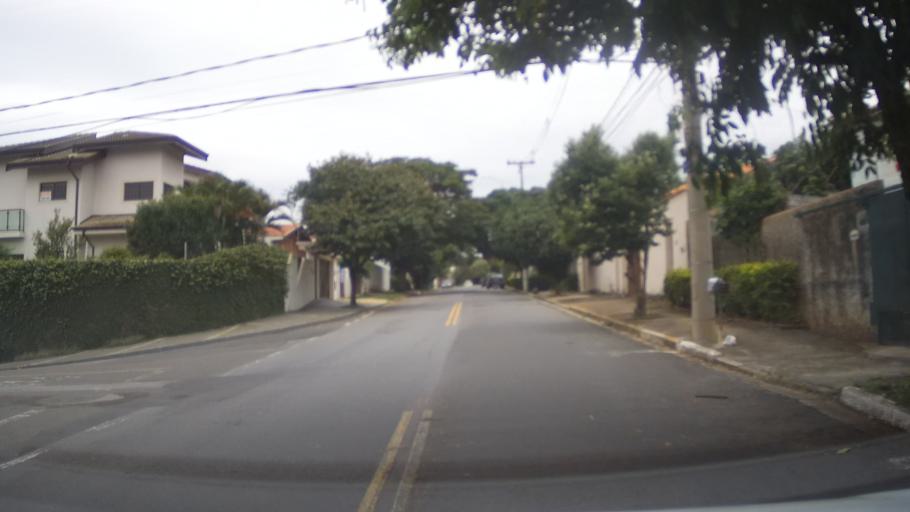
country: BR
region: Sao Paulo
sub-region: Campinas
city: Campinas
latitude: -22.8987
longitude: -47.0377
